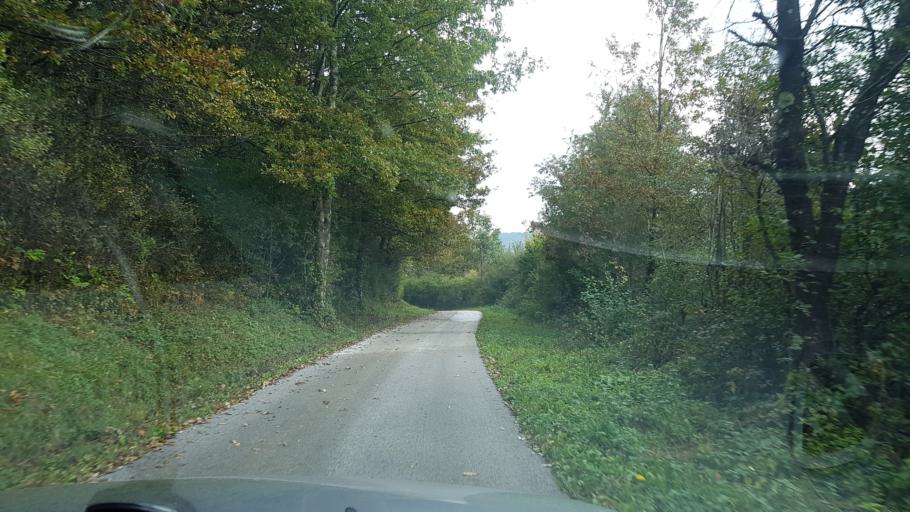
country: HR
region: Istarska
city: Buzet
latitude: 45.4168
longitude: 14.0893
